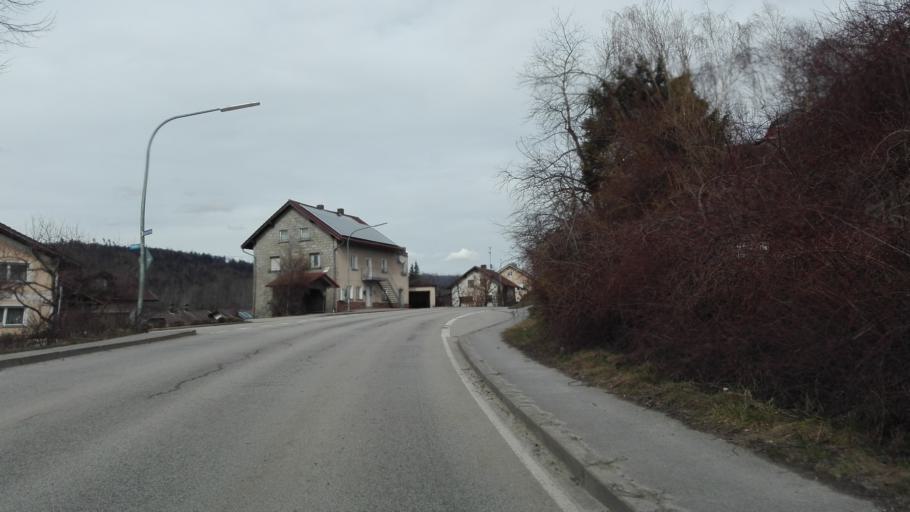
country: DE
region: Bavaria
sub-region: Lower Bavaria
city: Hauzenberg
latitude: 48.6423
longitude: 13.6011
